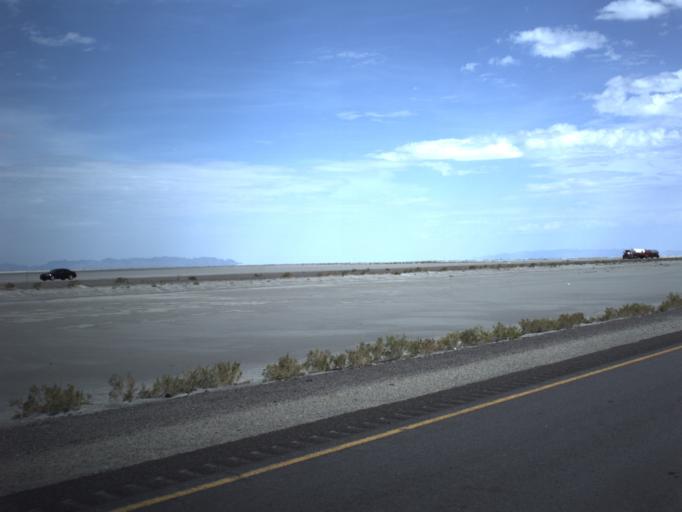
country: US
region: Utah
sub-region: Tooele County
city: Wendover
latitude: 40.7362
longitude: -113.7401
